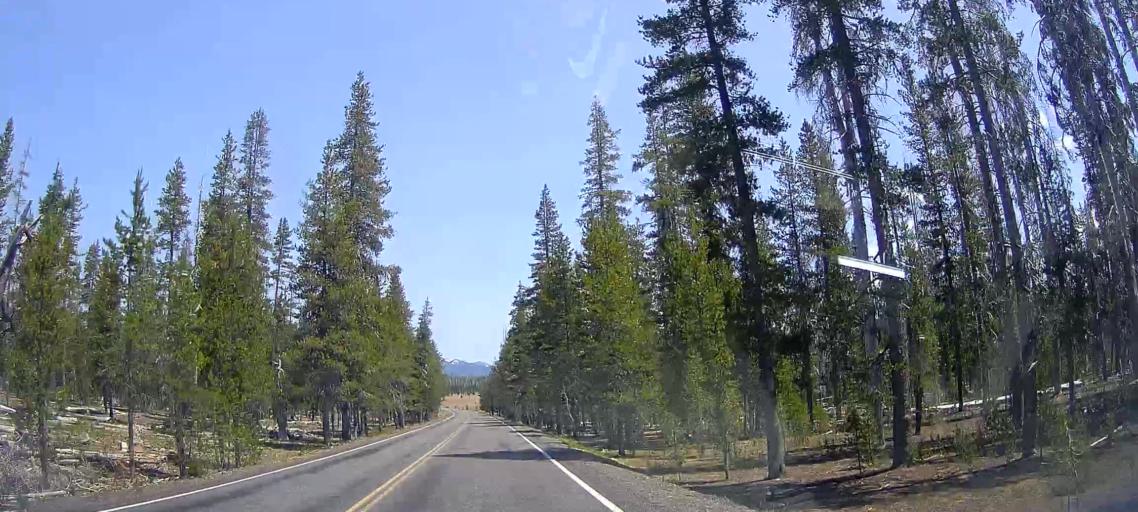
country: US
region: Oregon
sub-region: Lane County
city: Oakridge
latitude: 43.0252
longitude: -122.1204
